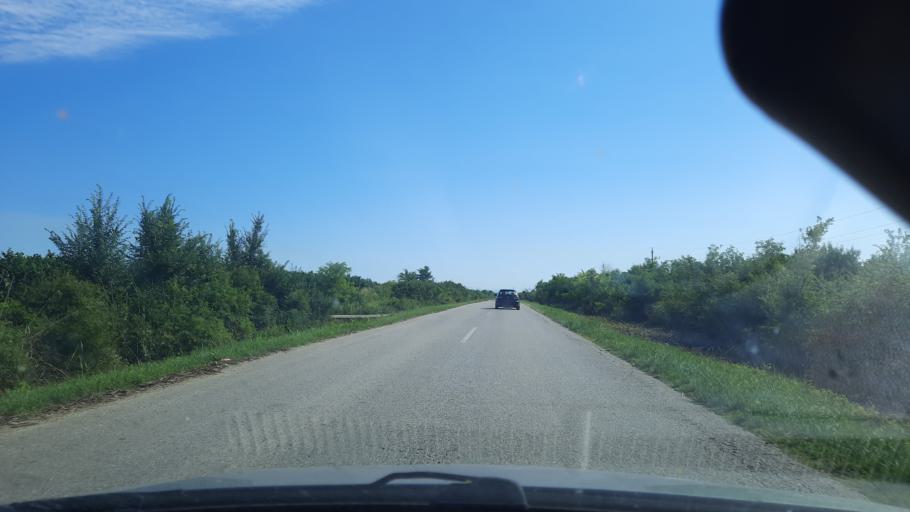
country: RS
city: Simanovci
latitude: 44.8033
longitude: 20.0983
